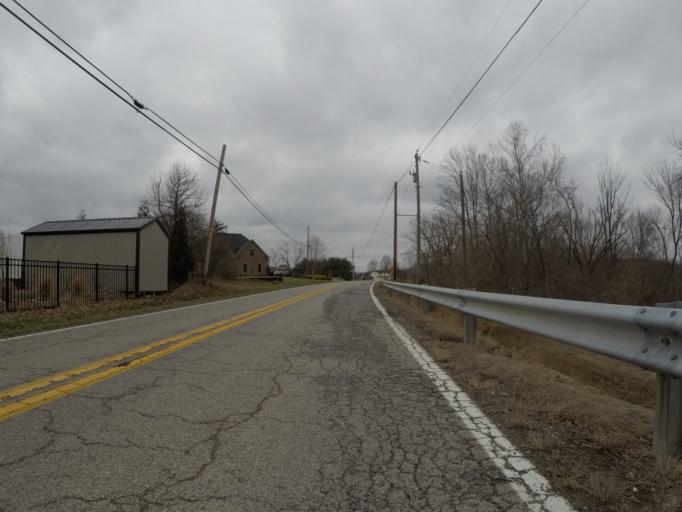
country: US
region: West Virginia
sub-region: Cabell County
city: Barboursville
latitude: 38.4273
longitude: -82.2402
